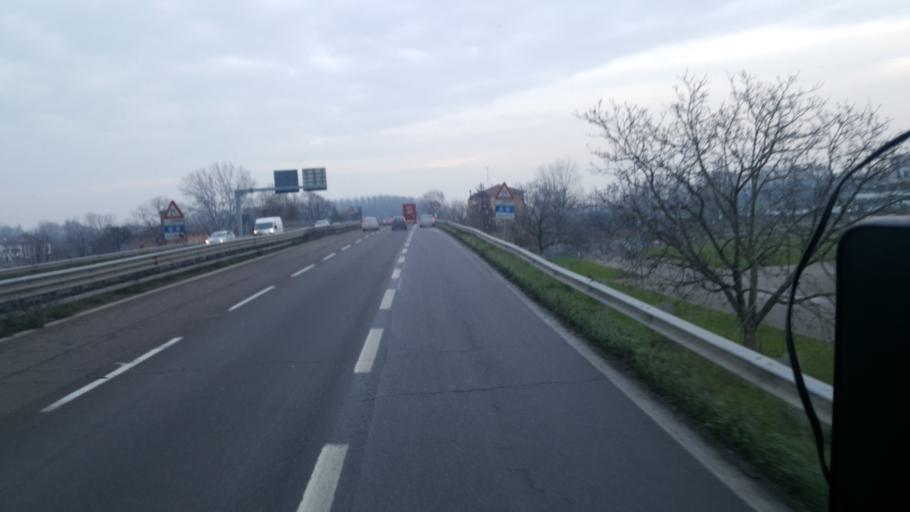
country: IT
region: Emilia-Romagna
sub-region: Provincia di Parma
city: Parma
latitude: 44.8217
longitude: 10.3121
